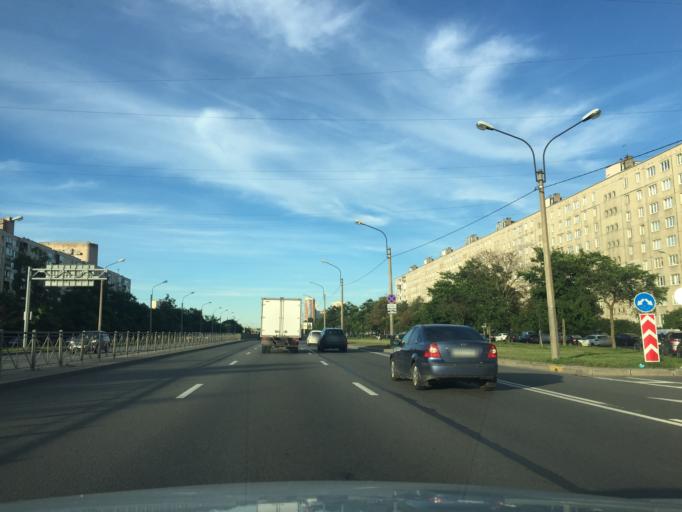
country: RU
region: St.-Petersburg
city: Shushary
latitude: 59.8392
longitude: 30.3982
